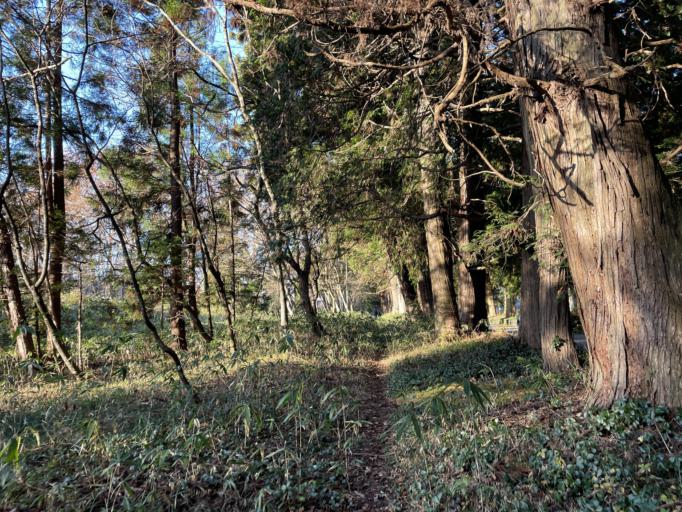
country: JP
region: Tochigi
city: Imaichi
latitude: 36.6541
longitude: 139.7217
